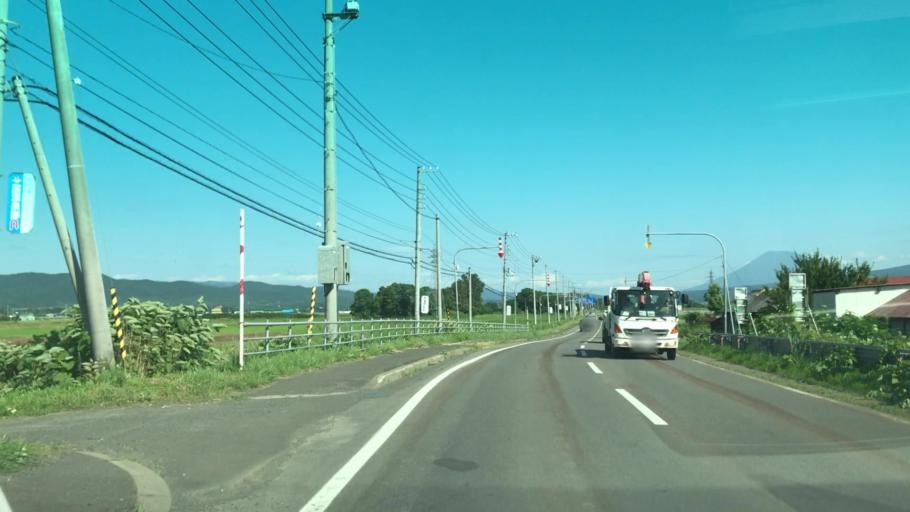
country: JP
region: Hokkaido
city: Iwanai
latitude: 43.0288
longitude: 140.5430
